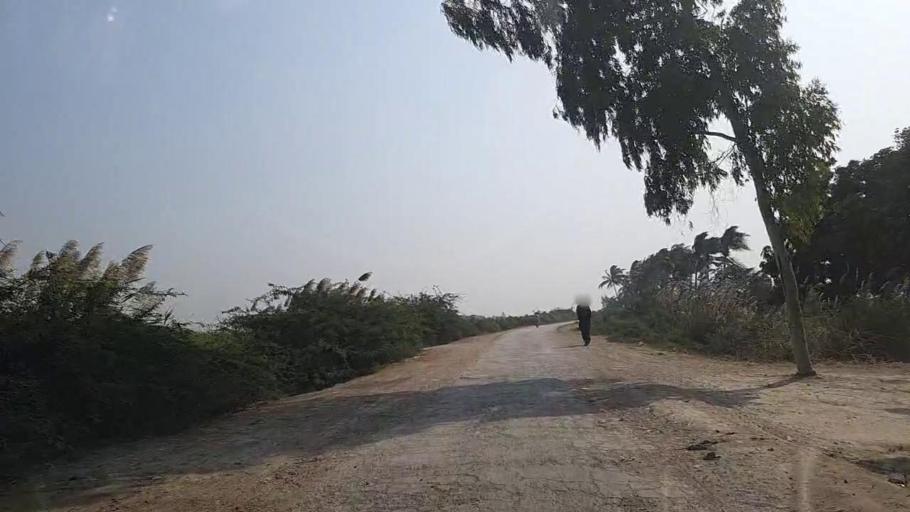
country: PK
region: Sindh
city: Keti Bandar
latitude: 24.2439
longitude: 67.6364
